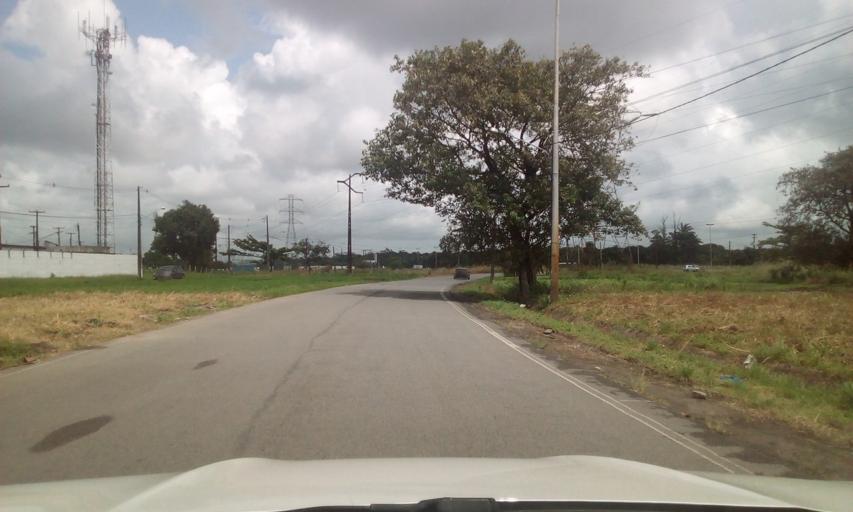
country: BR
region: Pernambuco
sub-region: Recife
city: Recife
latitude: -8.0691
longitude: -34.9436
